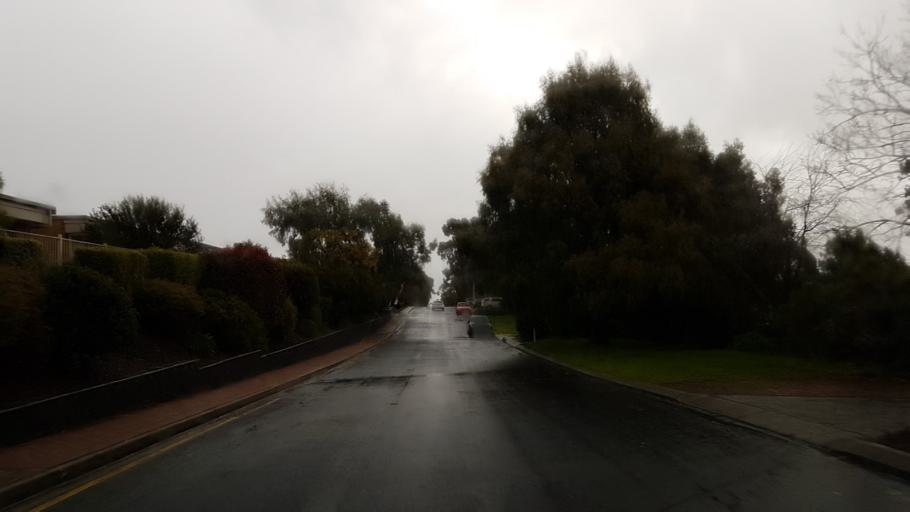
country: AU
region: South Australia
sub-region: Onkaparinga
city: Craigburn Farm
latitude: -35.0913
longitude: 138.5913
